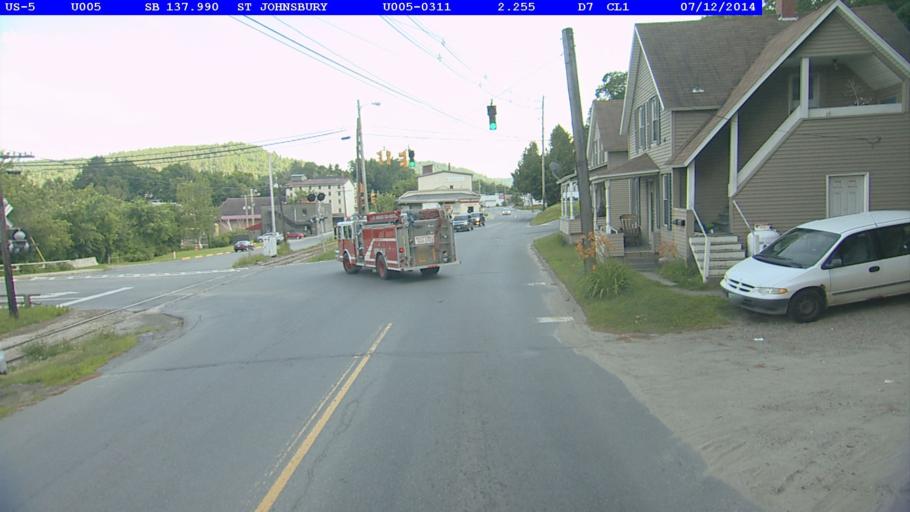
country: US
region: Vermont
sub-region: Caledonia County
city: St Johnsbury
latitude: 44.4257
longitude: -72.0149
